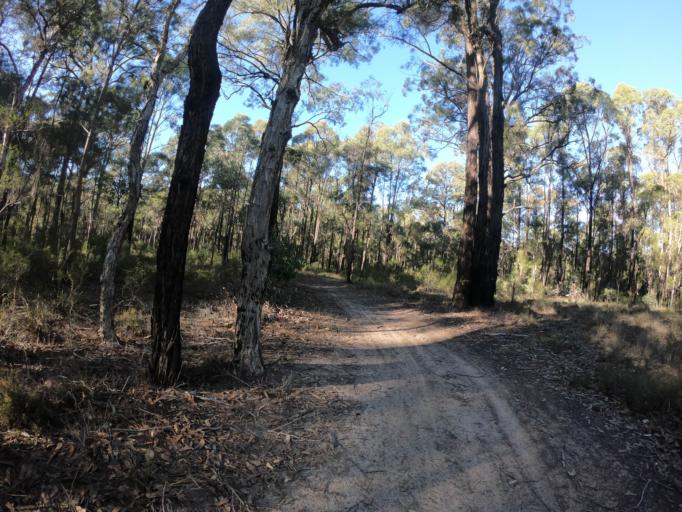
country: AU
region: New South Wales
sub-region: Hawkesbury
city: South Windsor
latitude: -33.6430
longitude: 150.7961
